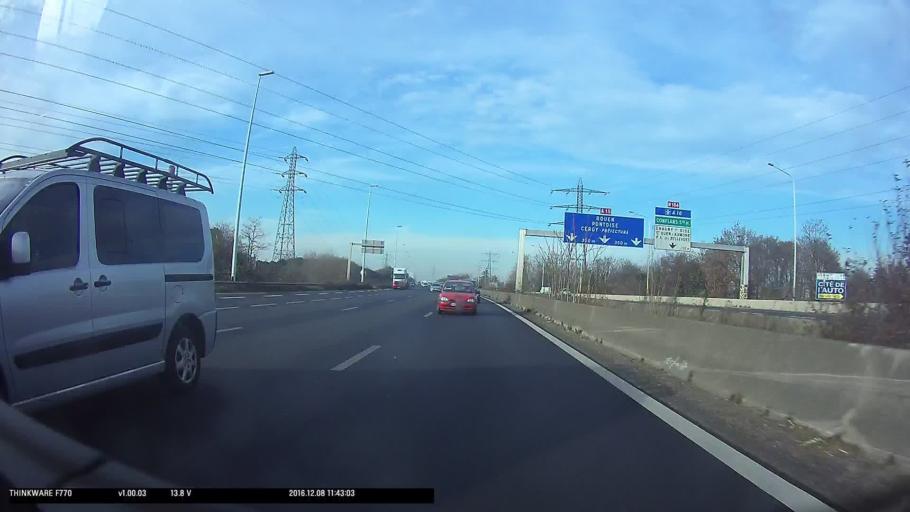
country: FR
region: Ile-de-France
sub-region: Departement du Val-d'Oise
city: Saint-Ouen-l'Aumone
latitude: 49.0311
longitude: 2.1208
